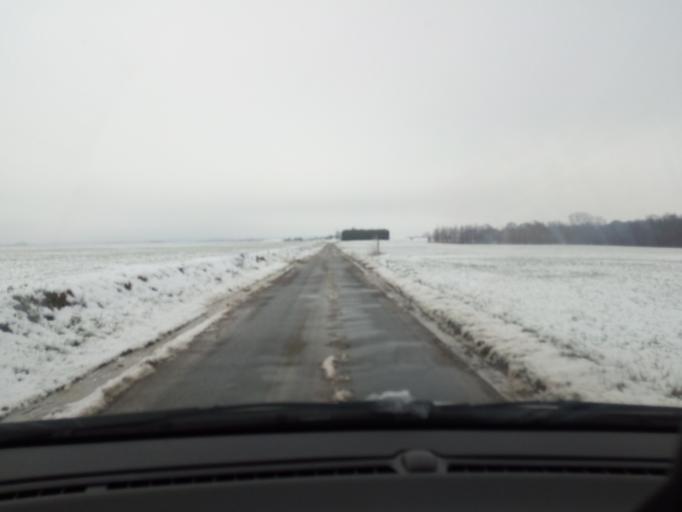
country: FR
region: Nord-Pas-de-Calais
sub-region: Departement du Nord
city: Boussois
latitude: 50.3561
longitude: 4.0255
